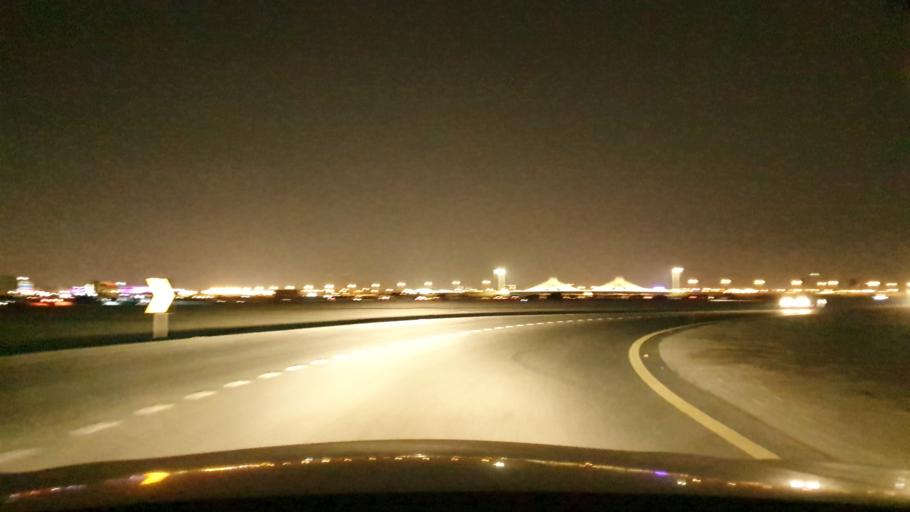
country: BH
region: Muharraq
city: Al Muharraq
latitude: 26.2558
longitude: 50.5823
